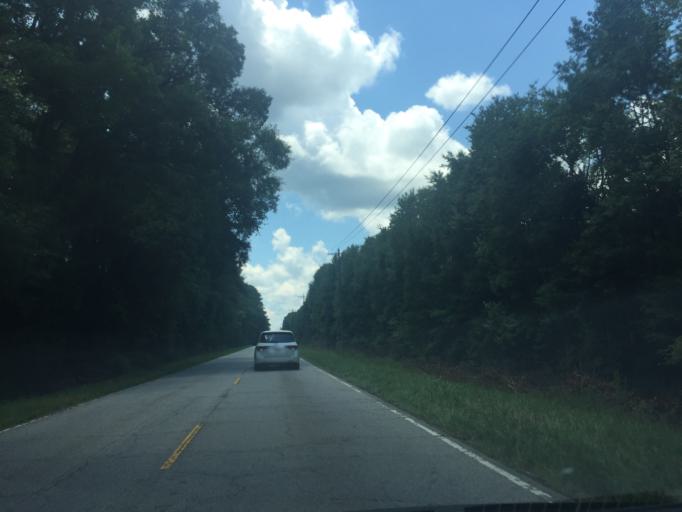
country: US
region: South Carolina
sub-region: Jasper County
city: Ridgeland
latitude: 32.4108
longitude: -81.0167
